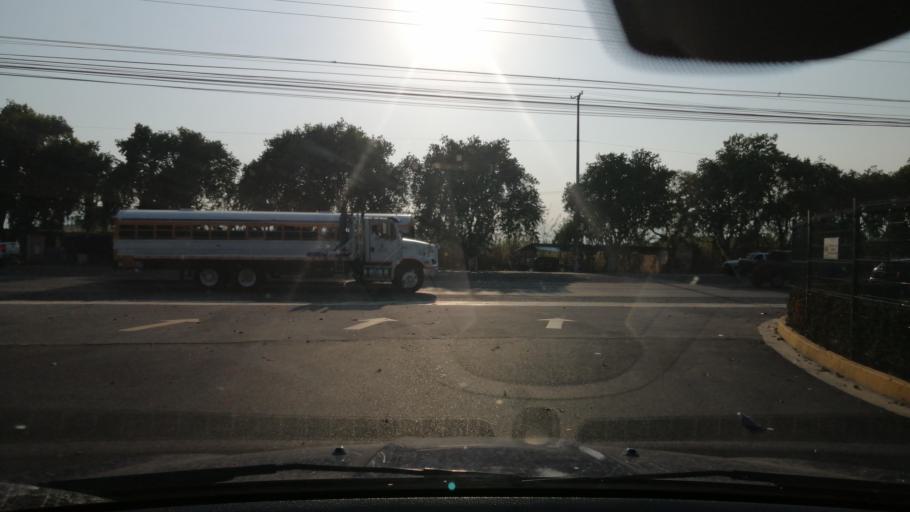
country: SV
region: La Libertad
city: Ciudad Arce
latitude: 13.7648
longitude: -89.3690
